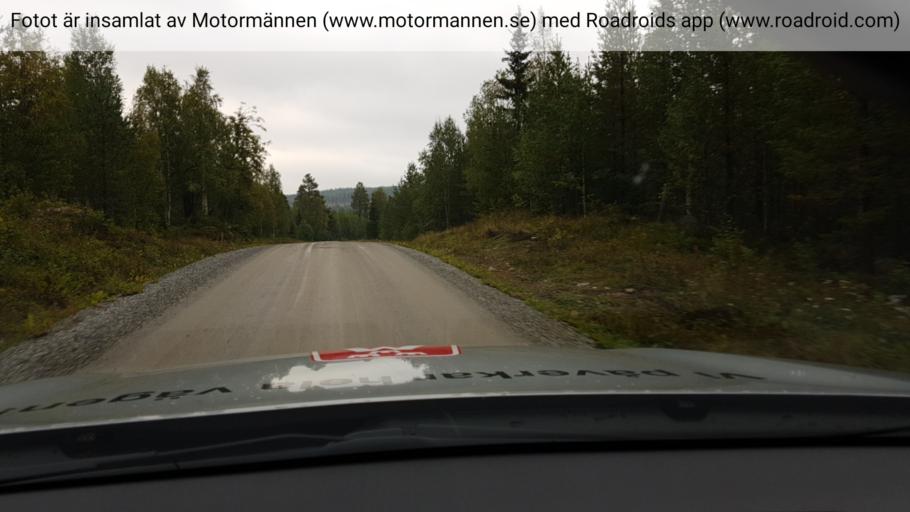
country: SE
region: Jaemtland
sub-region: Braecke Kommun
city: Braecke
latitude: 62.7395
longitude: 15.4935
